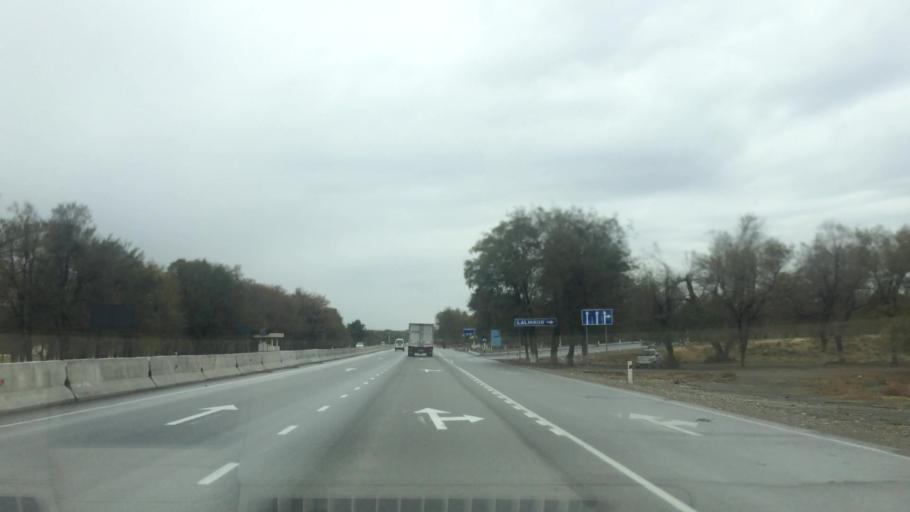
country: UZ
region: Samarqand
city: Bulung'ur
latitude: 39.9045
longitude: 67.5041
